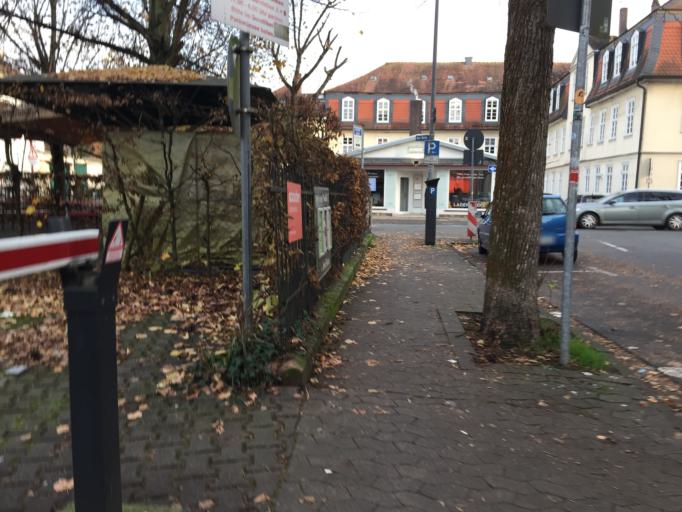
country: DE
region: Hesse
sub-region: Regierungsbezirk Giessen
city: Marburg an der Lahn
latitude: 50.8050
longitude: 8.7706
